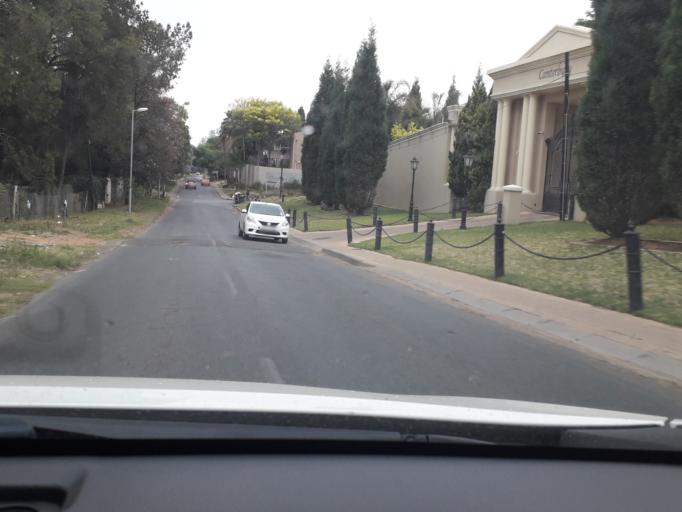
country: ZA
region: Gauteng
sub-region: City of Johannesburg Metropolitan Municipality
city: Johannesburg
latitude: -26.1161
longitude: 28.0433
